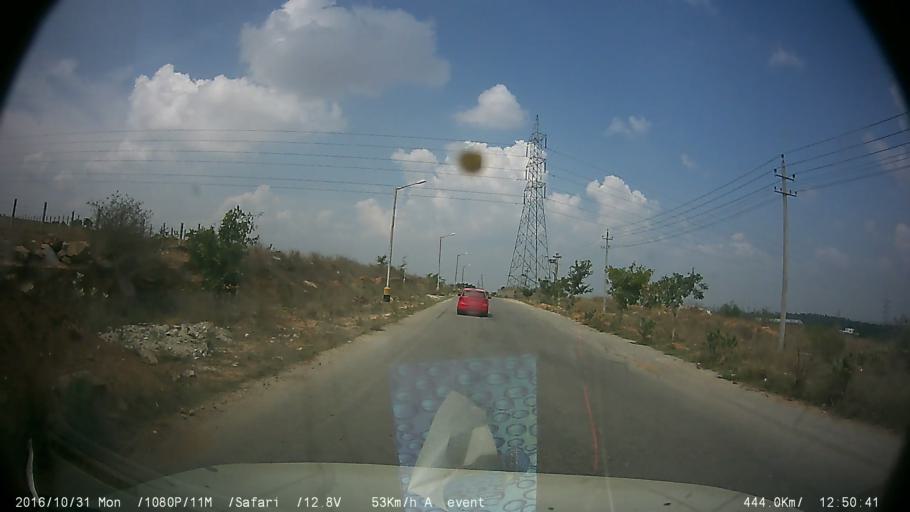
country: IN
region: Karnataka
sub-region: Mysore
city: Mysore
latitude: 12.3584
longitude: 76.5629
